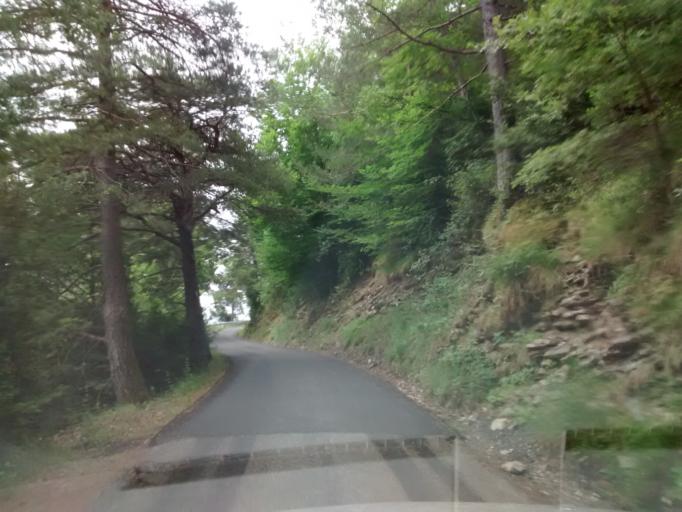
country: ES
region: Aragon
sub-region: Provincia de Huesca
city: Puertolas
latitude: 42.5695
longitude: 0.1396
